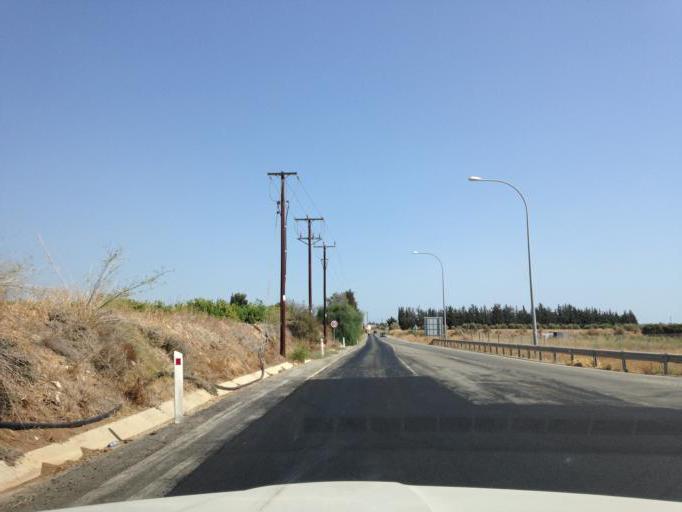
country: CY
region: Pafos
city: Mesogi
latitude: 34.7136
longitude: 32.5530
